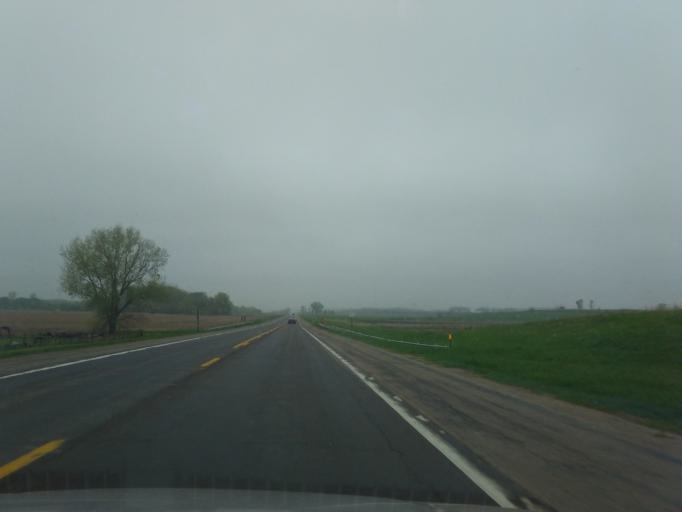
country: US
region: Nebraska
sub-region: Cuming County
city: Wisner
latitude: 41.9360
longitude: -96.8262
